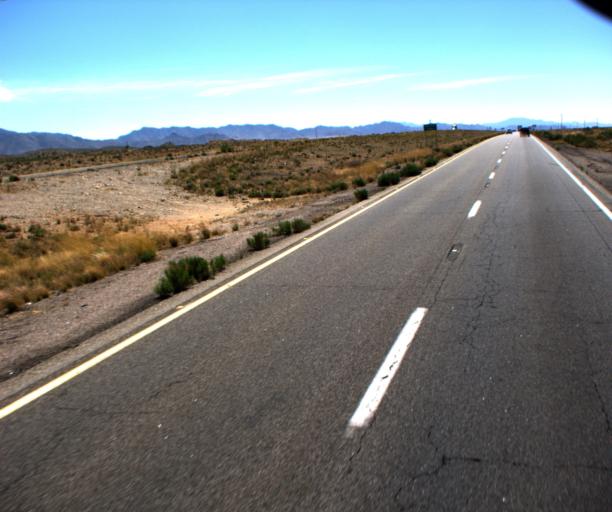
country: US
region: Arizona
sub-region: Mohave County
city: Dolan Springs
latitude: 35.4209
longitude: -114.2770
